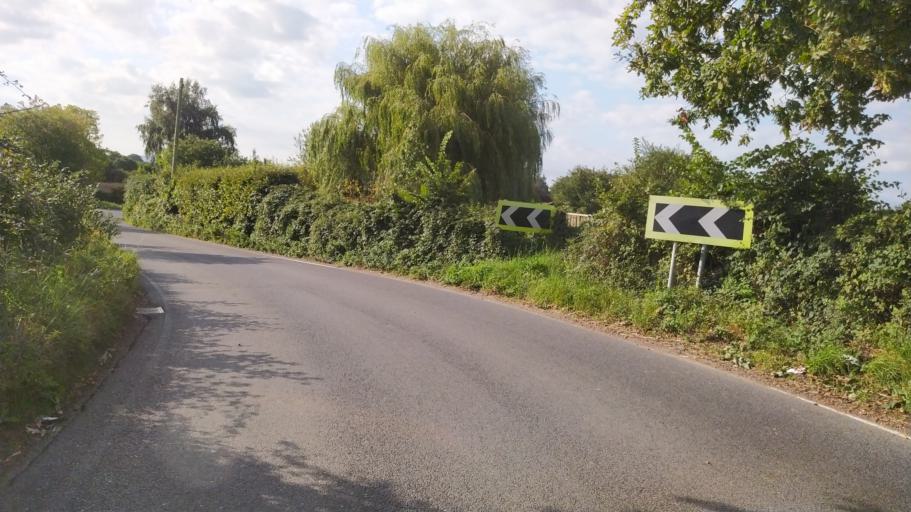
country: GB
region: England
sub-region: Dorset
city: Lytchett Matravers
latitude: 50.7434
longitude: -2.0480
